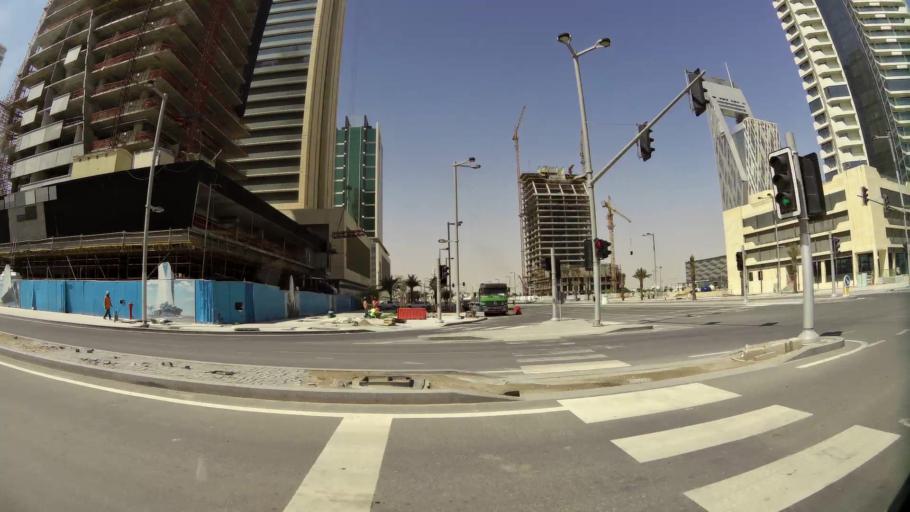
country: QA
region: Baladiyat ad Dawhah
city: Doha
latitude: 25.3901
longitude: 51.5234
